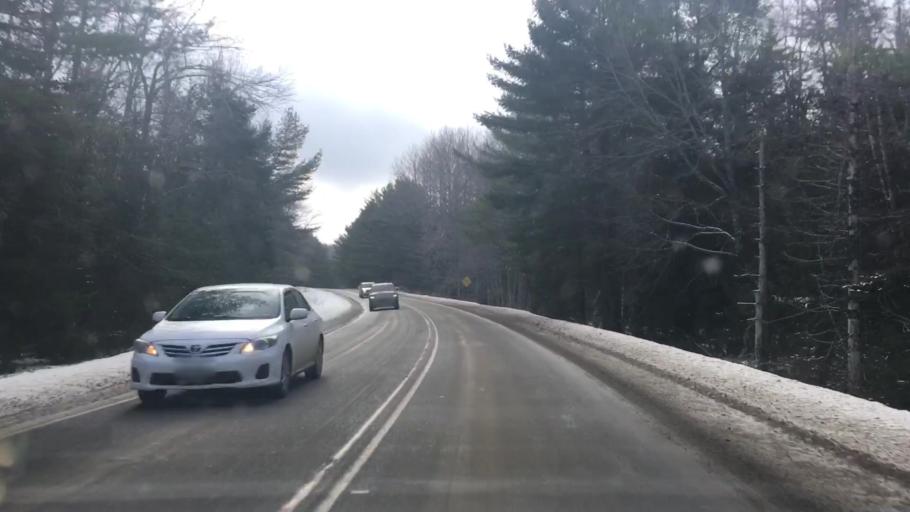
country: US
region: Maine
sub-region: Washington County
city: Calais
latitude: 45.0458
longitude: -67.3278
